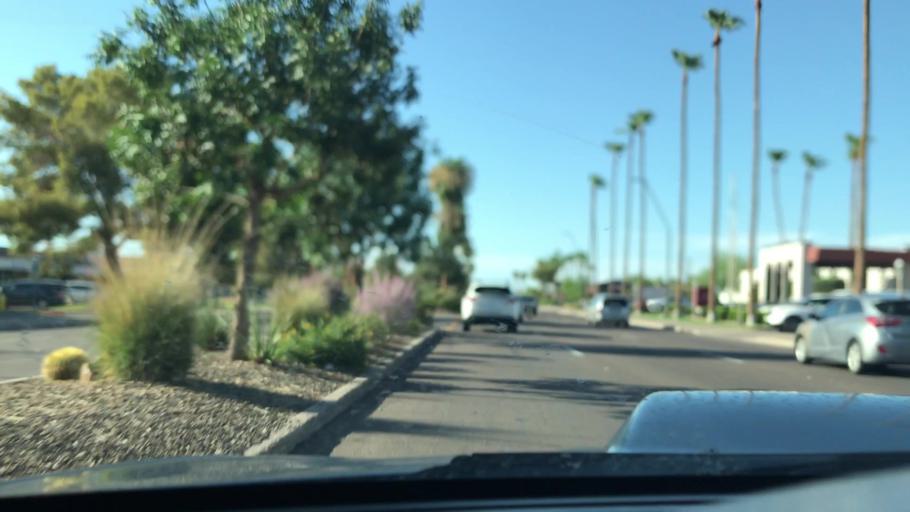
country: US
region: Arizona
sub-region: Maricopa County
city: Tempe
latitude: 33.4476
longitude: -111.9264
